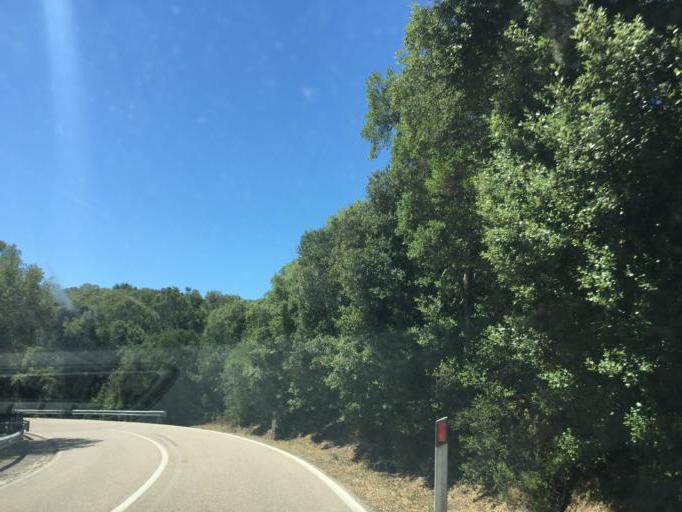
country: IT
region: Sardinia
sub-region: Provincia di Olbia-Tempio
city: Calangianus
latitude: 40.8940
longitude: 9.2651
